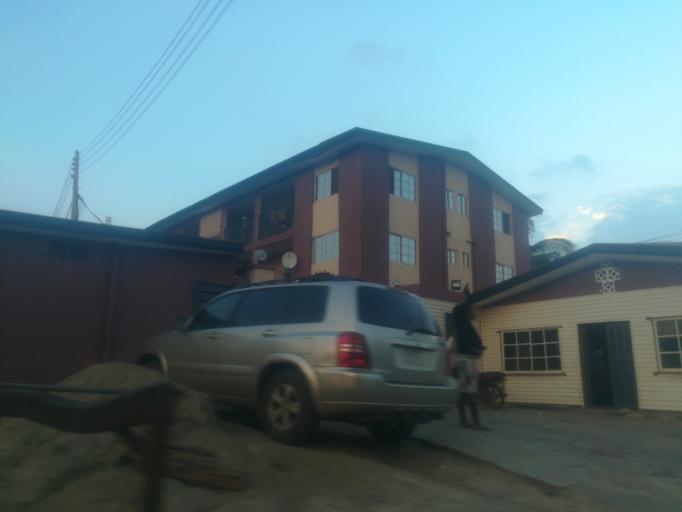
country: NG
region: Oyo
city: Ibadan
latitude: 7.4321
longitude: 3.9334
